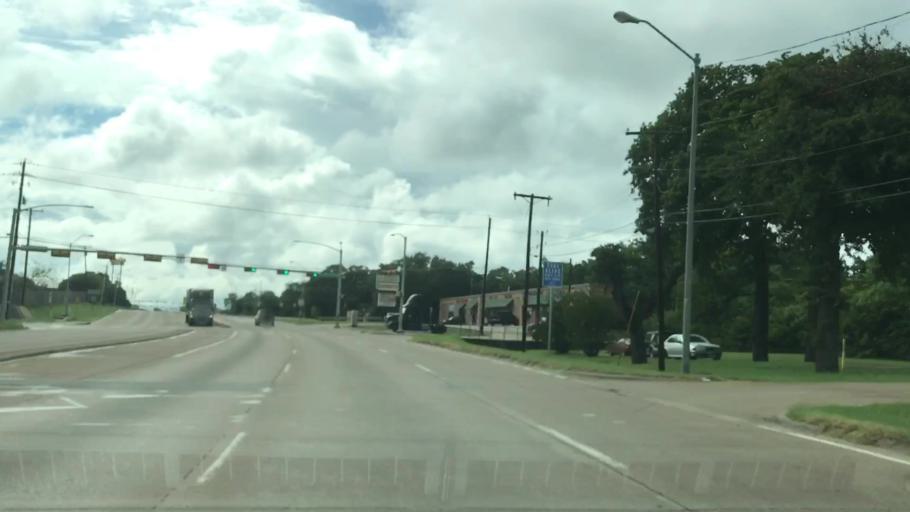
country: US
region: Texas
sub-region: Dallas County
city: Irving
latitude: 32.8097
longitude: -96.9161
